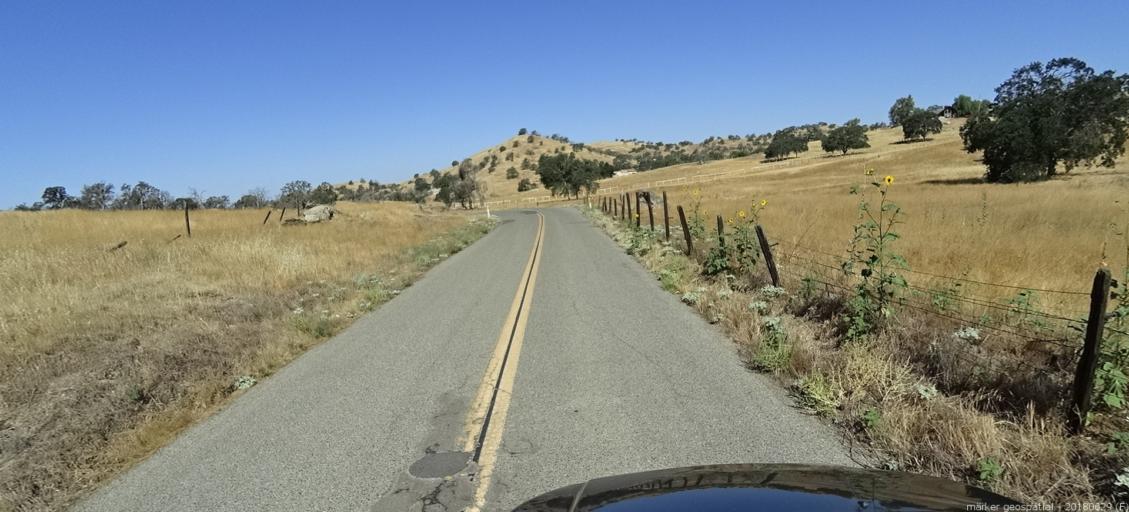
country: US
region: California
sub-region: Madera County
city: Bonadelle Ranchos-Madera Ranchos
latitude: 37.0792
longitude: -119.8271
